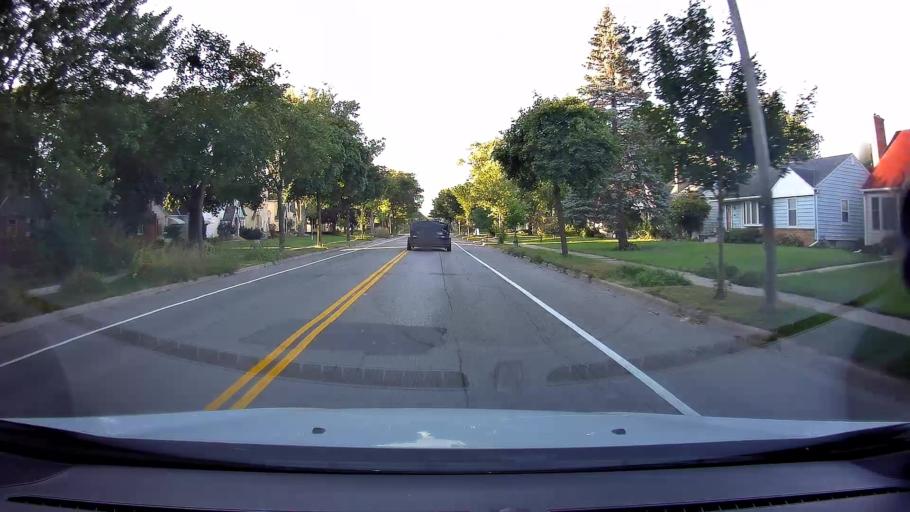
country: US
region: Minnesota
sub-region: Hennepin County
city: Richfield
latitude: 44.9227
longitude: -93.2473
